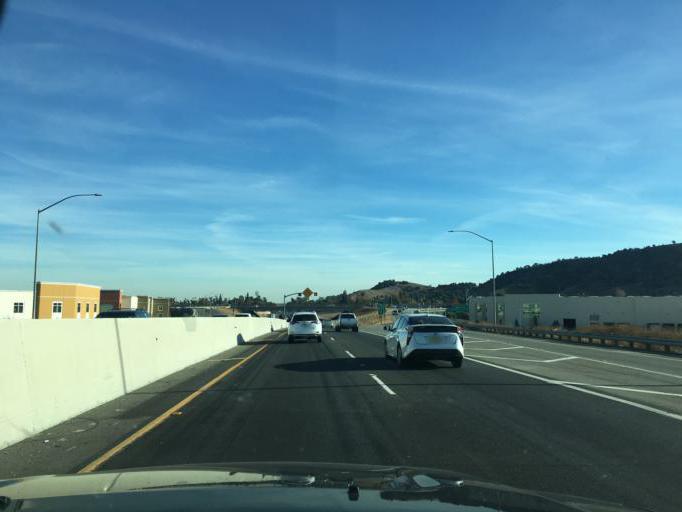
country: US
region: California
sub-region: Los Angeles County
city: Pomona
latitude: 34.0562
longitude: -117.7840
